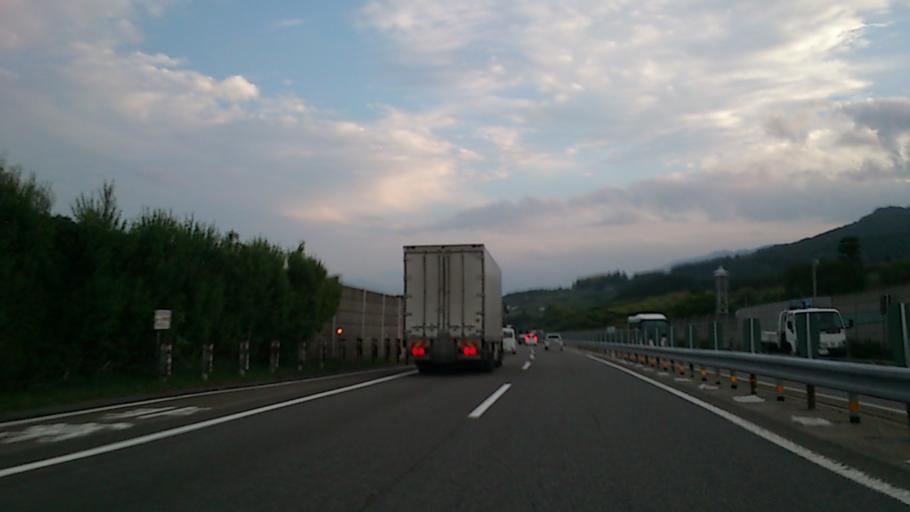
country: JP
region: Nagano
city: Iida
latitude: 35.5544
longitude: 137.8521
